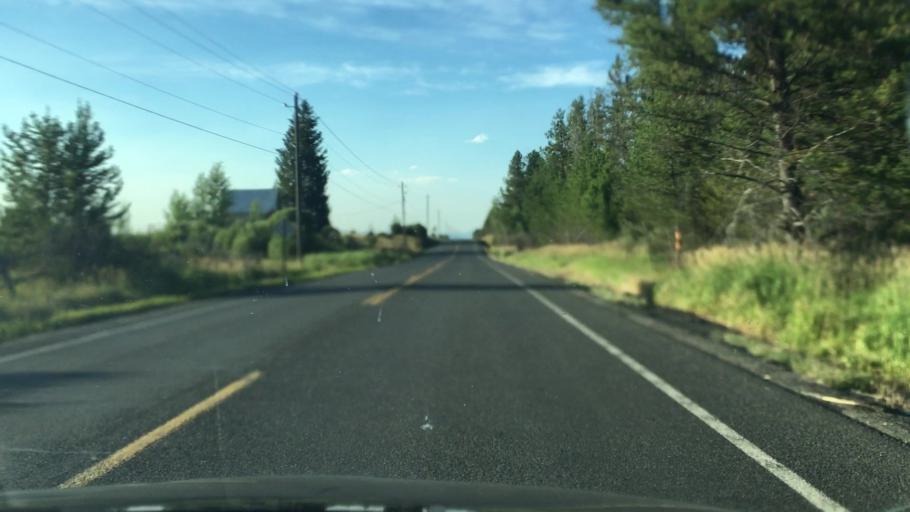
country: US
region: Idaho
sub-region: Valley County
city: McCall
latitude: 44.7930
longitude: -116.0782
